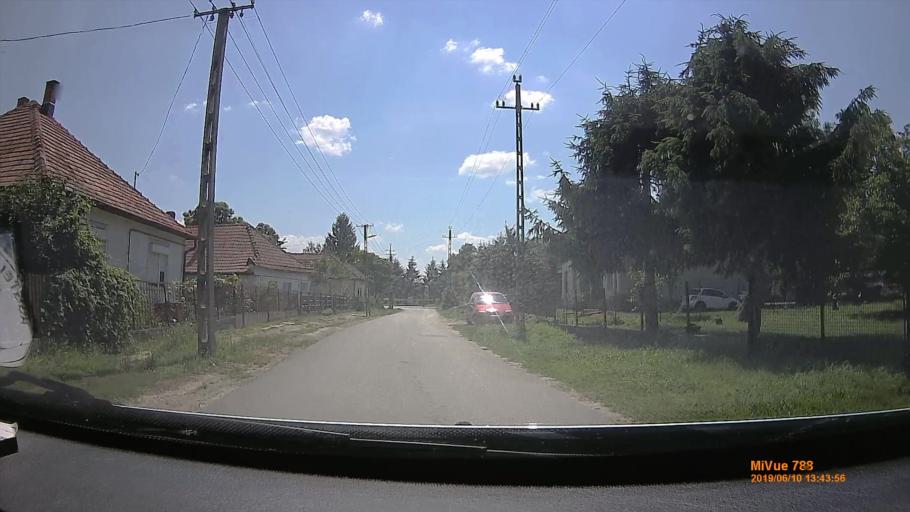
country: HU
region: Szabolcs-Szatmar-Bereg
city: Tiszadob
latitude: 48.0136
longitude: 21.1683
